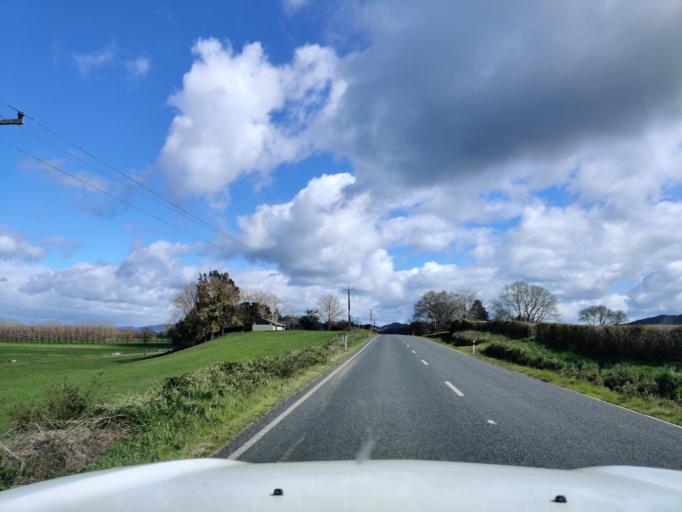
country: NZ
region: Waikato
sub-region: Waikato District
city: Ngaruawahia
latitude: -37.5719
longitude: 175.2505
